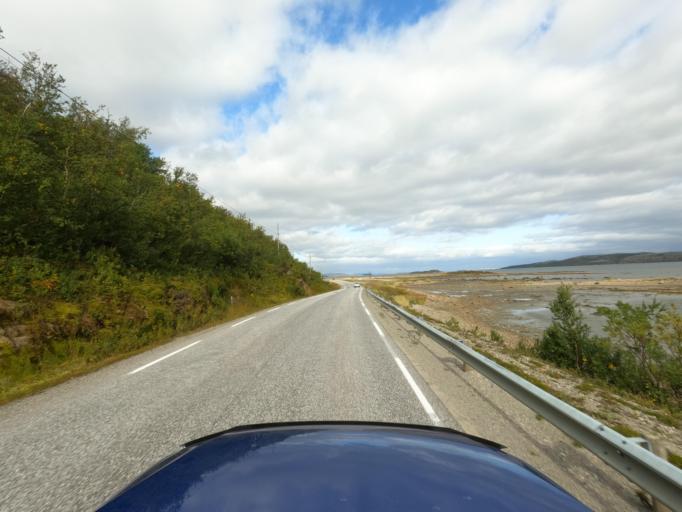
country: NO
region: Finnmark Fylke
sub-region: Porsanger
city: Lakselv
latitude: 70.1103
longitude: 24.9186
